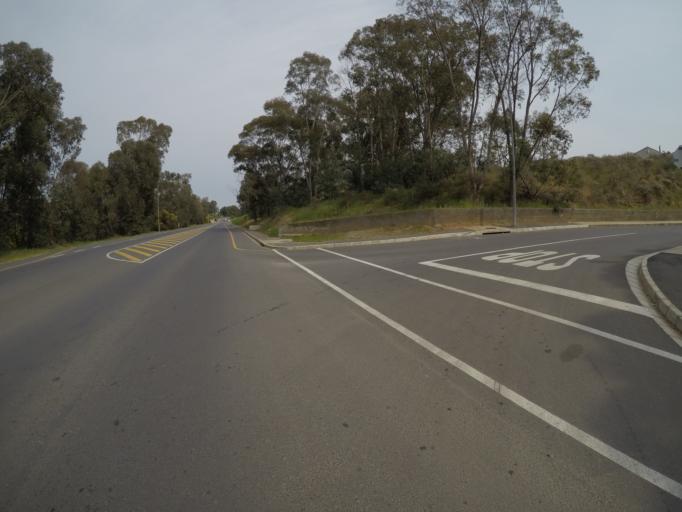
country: ZA
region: Western Cape
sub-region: West Coast District Municipality
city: Malmesbury
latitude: -33.4620
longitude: 18.7422
